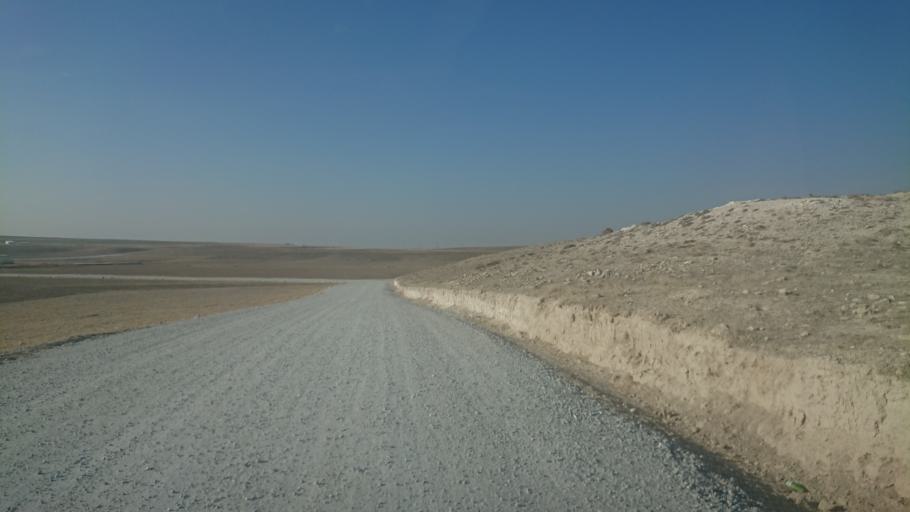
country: TR
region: Aksaray
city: Sultanhani
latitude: 38.0825
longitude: 33.6221
